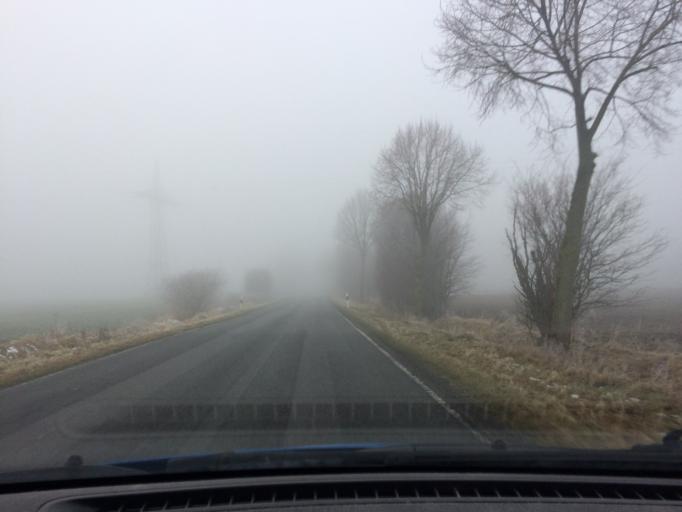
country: DE
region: Schleswig-Holstein
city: Kruzen
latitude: 53.3926
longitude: 10.5285
